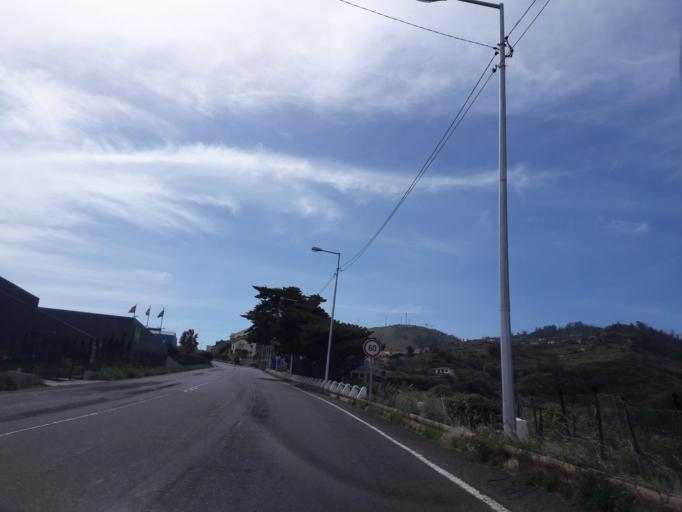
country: PT
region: Madeira
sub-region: Santa Cruz
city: Santa Cruz
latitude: 32.6602
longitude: -16.8142
